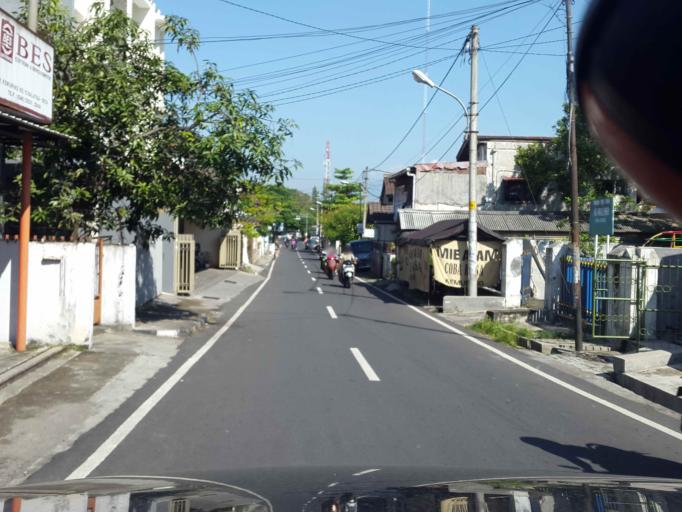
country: ID
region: Central Java
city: Salatiga
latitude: -7.3293
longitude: 110.5026
